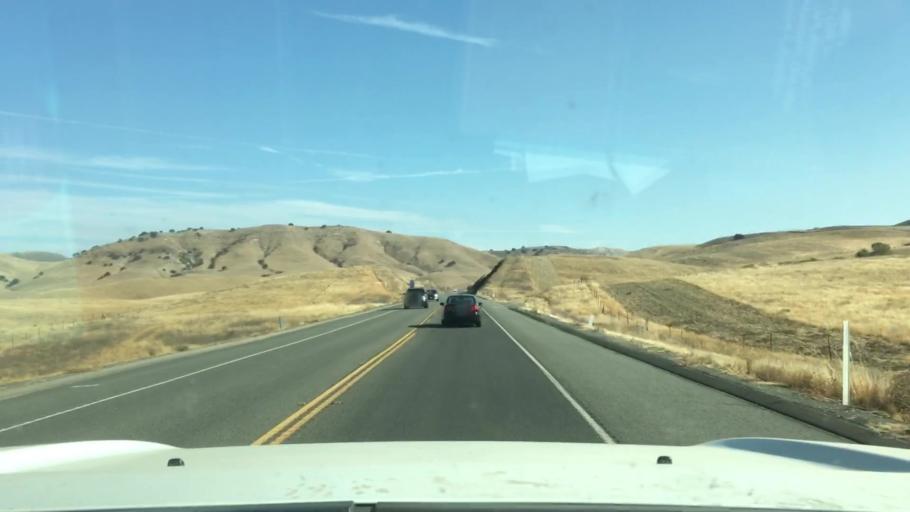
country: US
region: California
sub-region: San Luis Obispo County
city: Shandon
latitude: 35.7426
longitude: -120.2403
